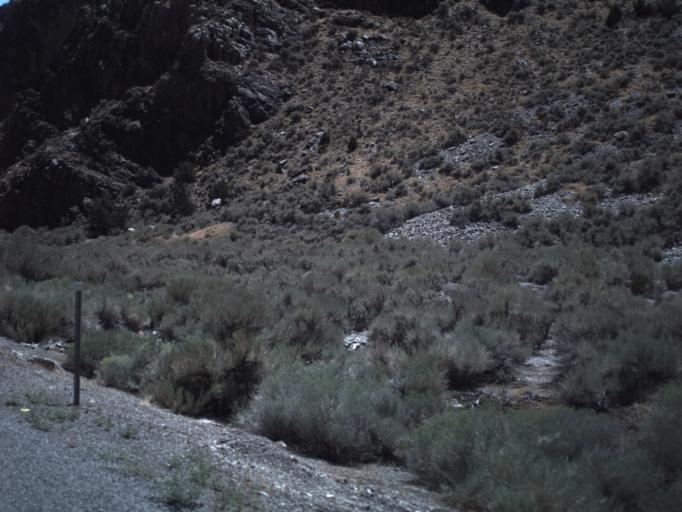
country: US
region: Utah
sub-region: Beaver County
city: Milford
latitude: 39.0871
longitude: -113.5657
